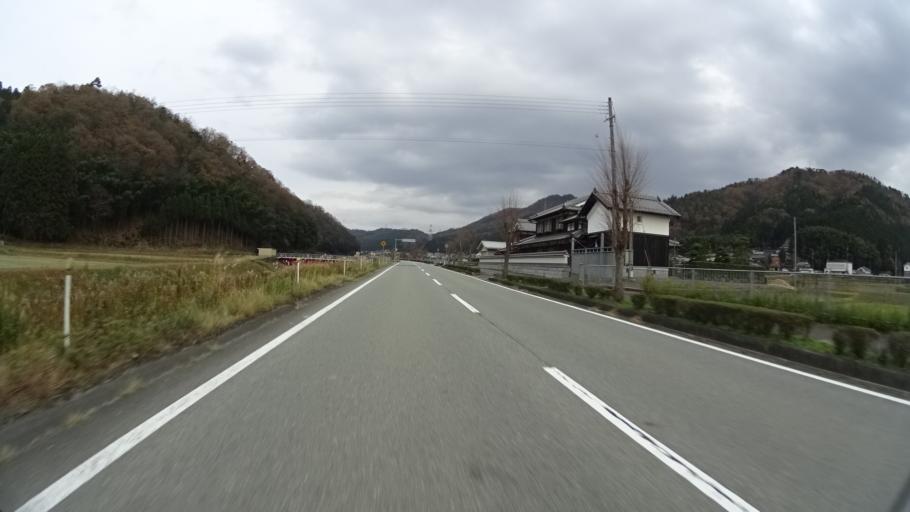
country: JP
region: Hyogo
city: Sasayama
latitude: 35.0739
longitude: 135.3566
